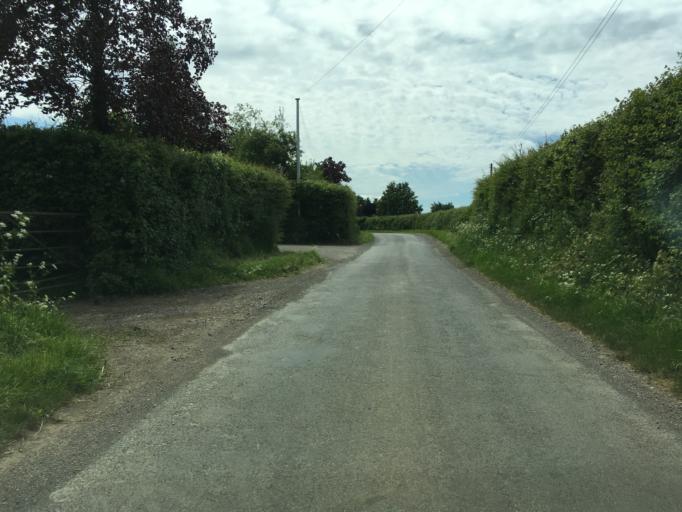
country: GB
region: England
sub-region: South Gloucestershire
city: Charfield
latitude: 51.6646
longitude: -2.4105
